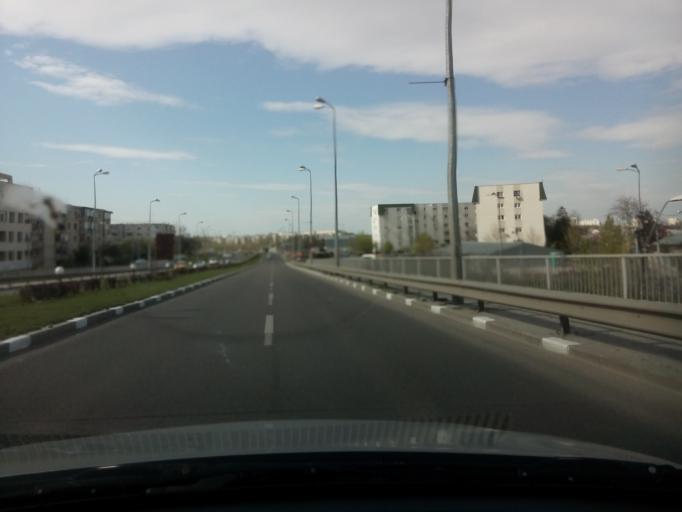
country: RO
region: Ilfov
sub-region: Comuna Fundeni-Dobroesti
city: Fundeni
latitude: 44.4499
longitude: 26.1531
